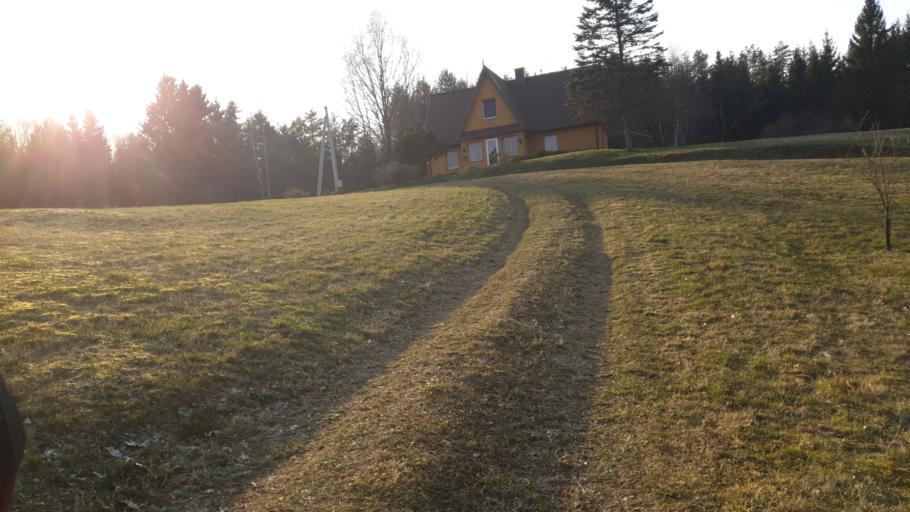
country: LT
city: Nemencine
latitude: 54.8761
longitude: 25.5756
